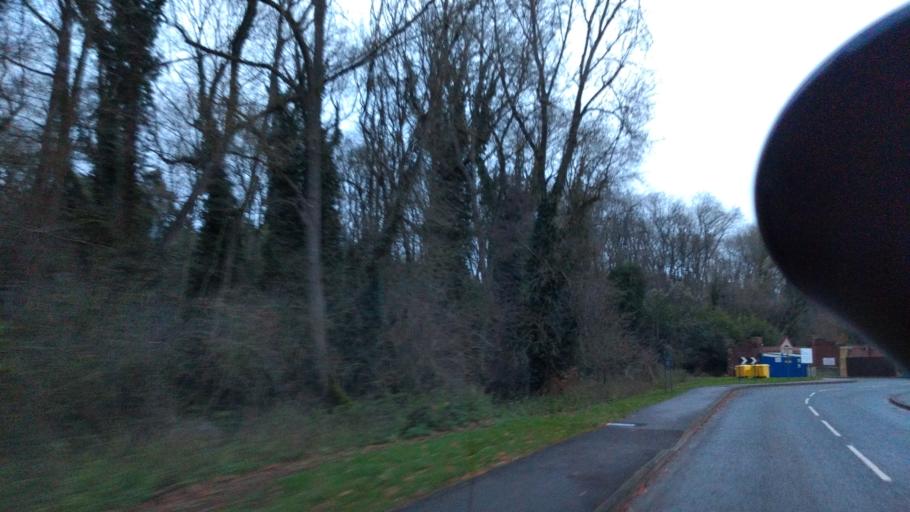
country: GB
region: England
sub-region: Oxfordshire
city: Shrivenham
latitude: 51.6045
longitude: -1.6423
